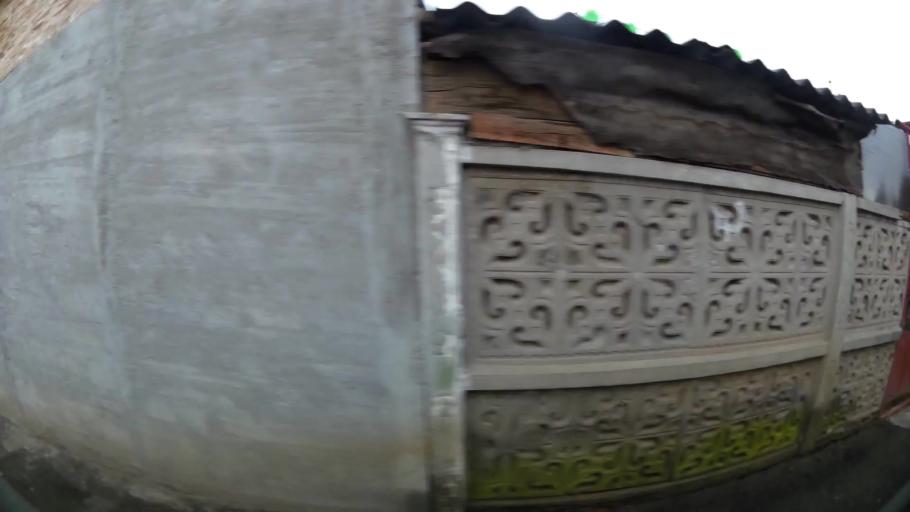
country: RO
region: Ilfov
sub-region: Comuna Pantelimon
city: Pantelimon
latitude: 44.4492
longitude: 26.2113
